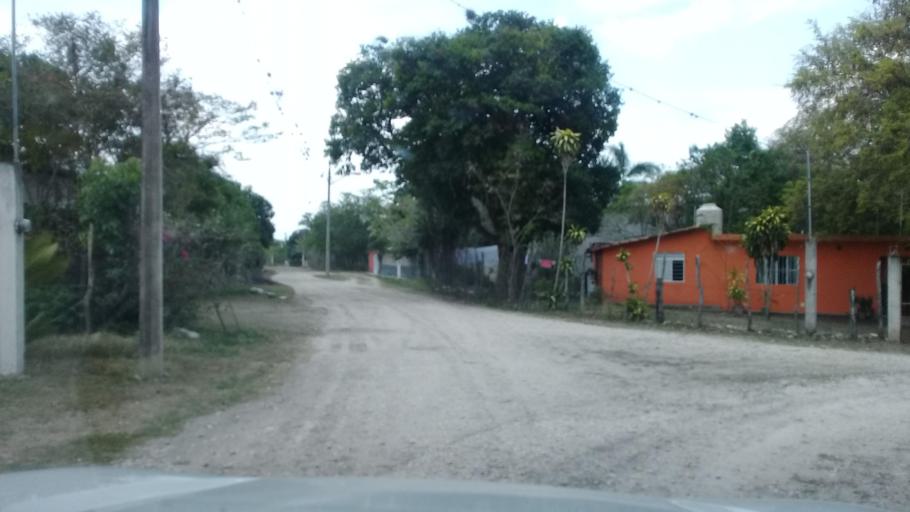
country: MX
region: Veracruz
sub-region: Emiliano Zapata
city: Plan del Rio
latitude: 19.3542
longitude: -96.6453
